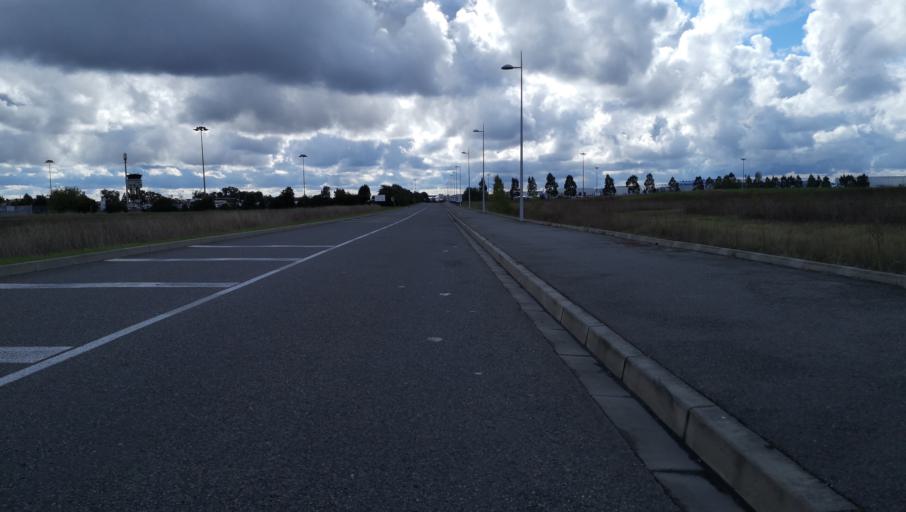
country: FR
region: Midi-Pyrenees
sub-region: Departement de la Haute-Garonne
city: Beauzelle
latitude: 43.6427
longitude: 1.3648
